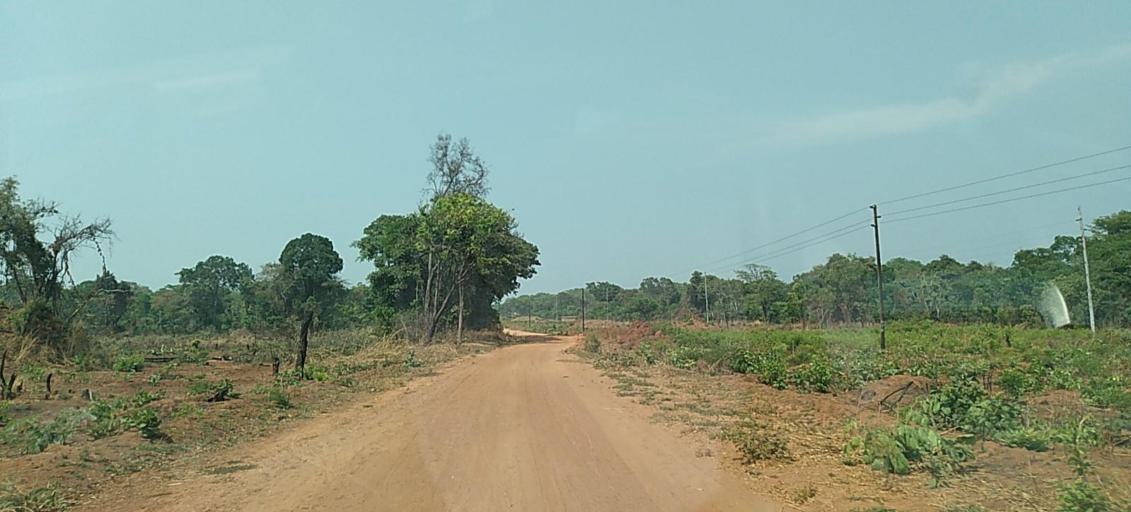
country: ZM
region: Copperbelt
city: Chingola
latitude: -13.0486
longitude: 27.4311
